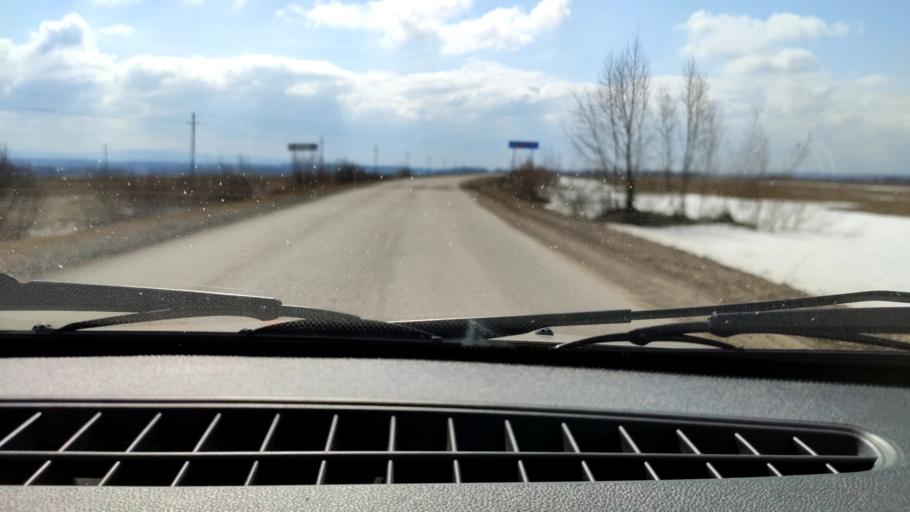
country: RU
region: Bashkortostan
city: Kudeyevskiy
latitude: 54.8438
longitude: 56.7955
